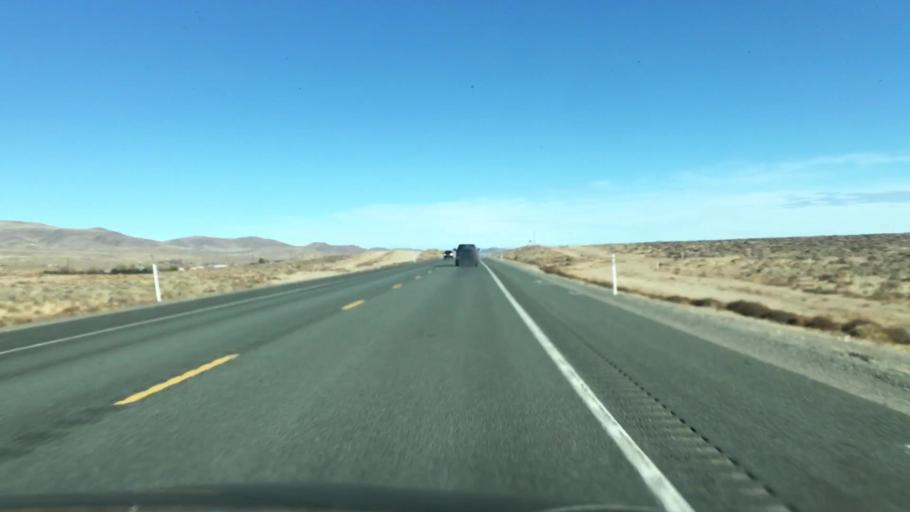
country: US
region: Nevada
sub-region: Lyon County
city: Stagecoach
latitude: 39.3792
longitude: -119.3259
